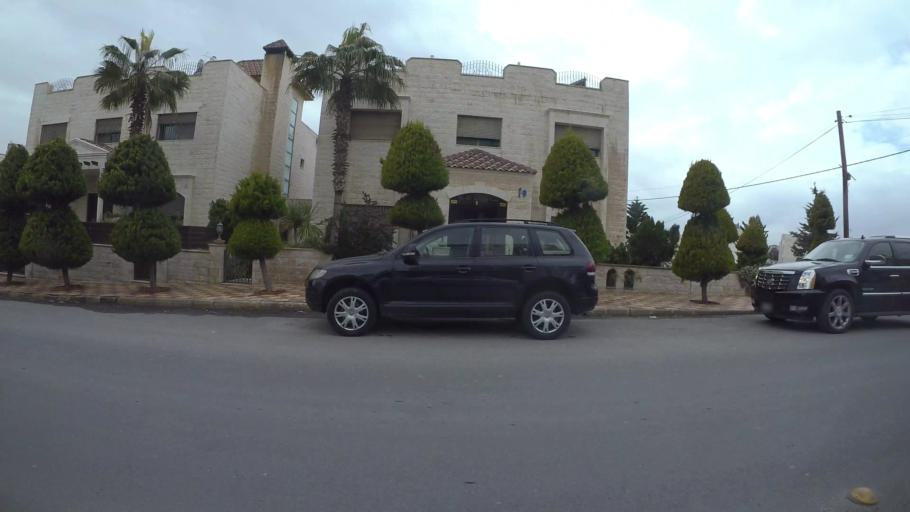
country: JO
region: Amman
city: Wadi as Sir
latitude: 31.9851
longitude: 35.8373
